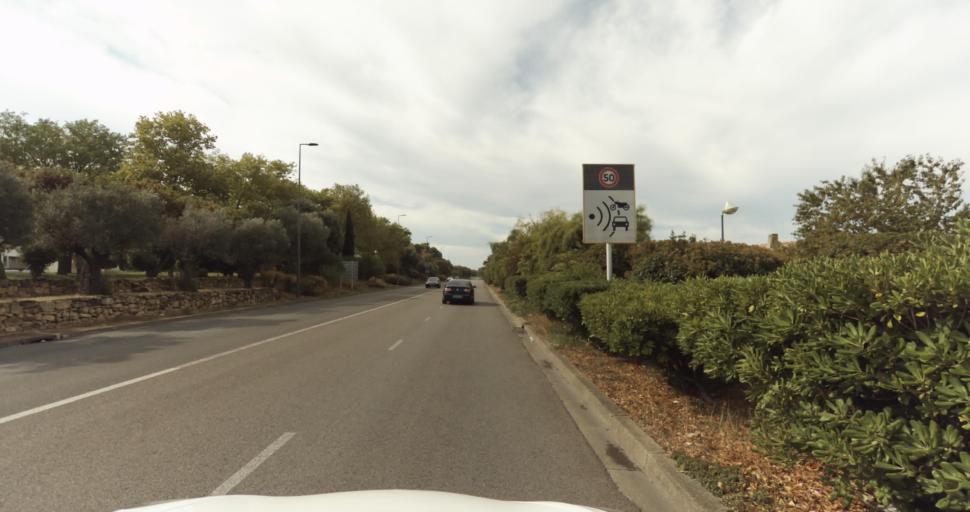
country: FR
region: Provence-Alpes-Cote d'Azur
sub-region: Departement des Bouches-du-Rhone
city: Miramas
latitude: 43.5977
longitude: 5.0056
